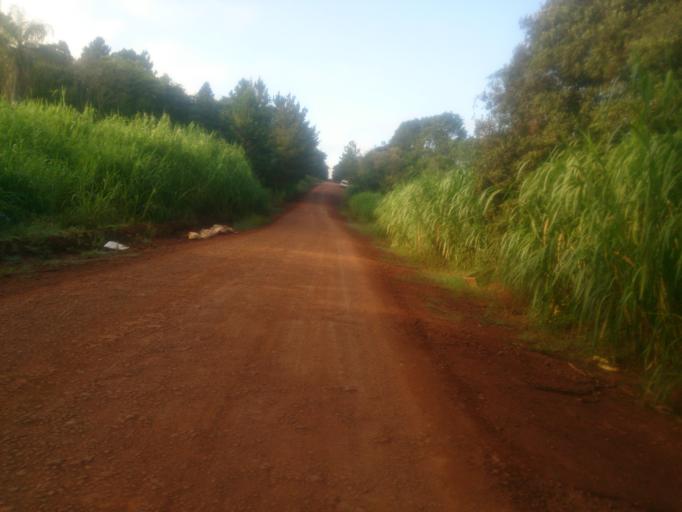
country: AR
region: Misiones
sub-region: Departamento de Obera
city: Obera
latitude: -27.4646
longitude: -55.1062
